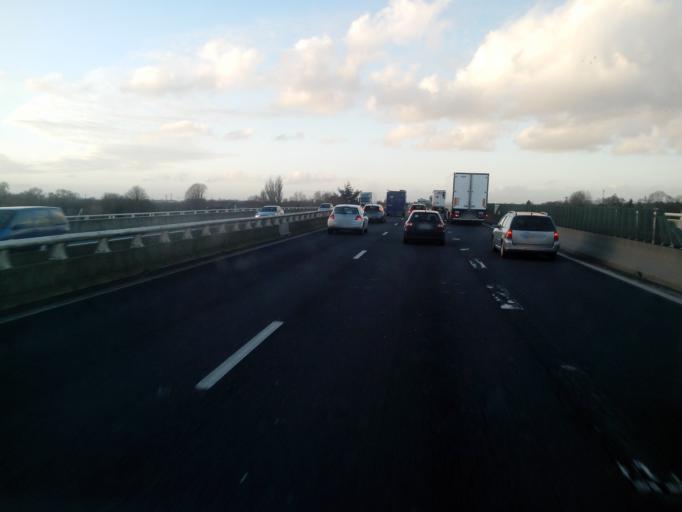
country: FR
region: Pays de la Loire
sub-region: Departement de la Loire-Atlantique
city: Basse-Goulaine
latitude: 47.2314
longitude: -1.4715
